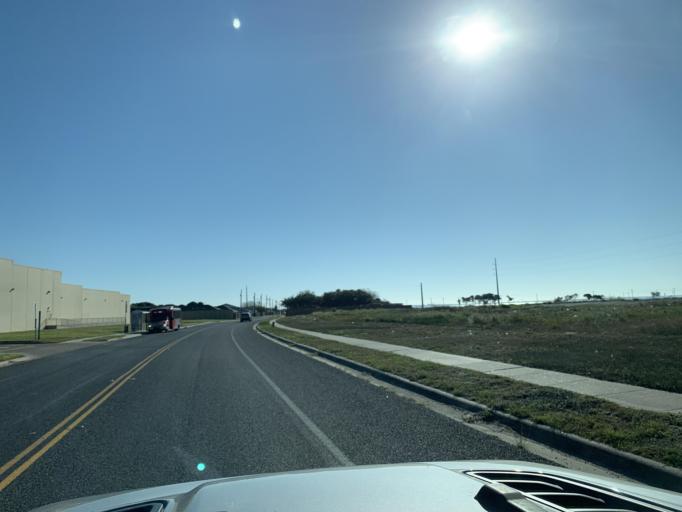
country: US
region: Texas
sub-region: Nueces County
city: Corpus Christi
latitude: 27.6646
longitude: -97.2822
